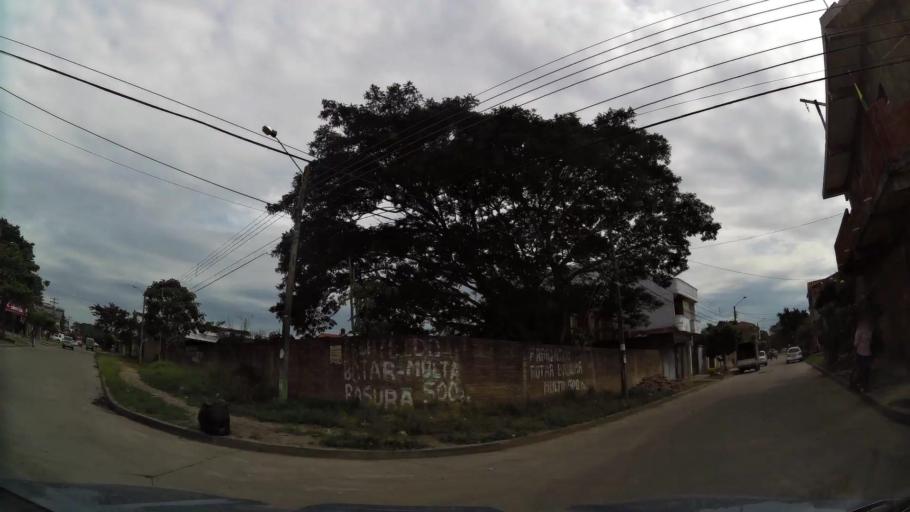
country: BO
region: Santa Cruz
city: Santa Cruz de la Sierra
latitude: -17.7793
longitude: -63.2150
